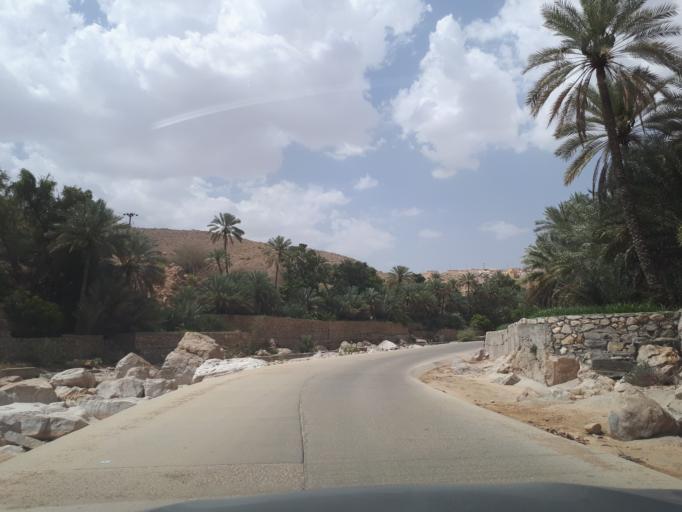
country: OM
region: Ash Sharqiyah
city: Badiyah
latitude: 22.6095
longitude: 59.0912
